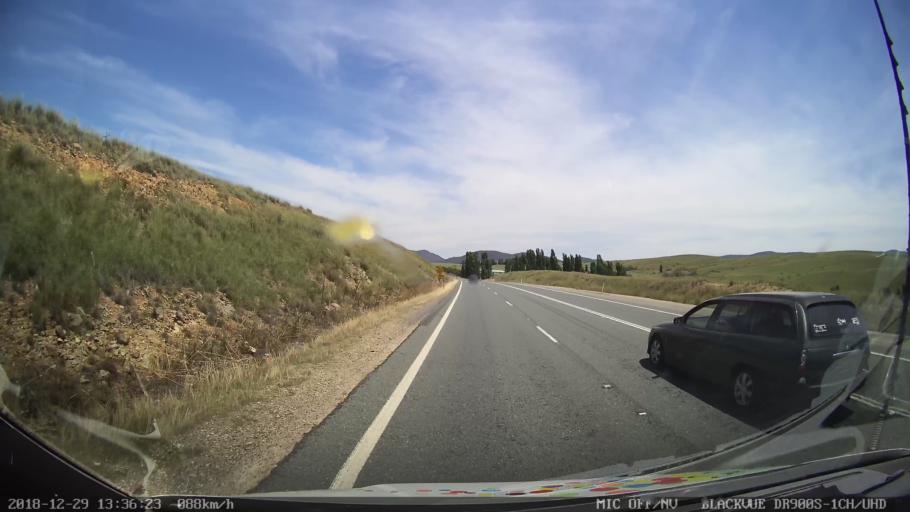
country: AU
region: New South Wales
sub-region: Cooma-Monaro
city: Cooma
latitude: -35.9698
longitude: 149.1415
